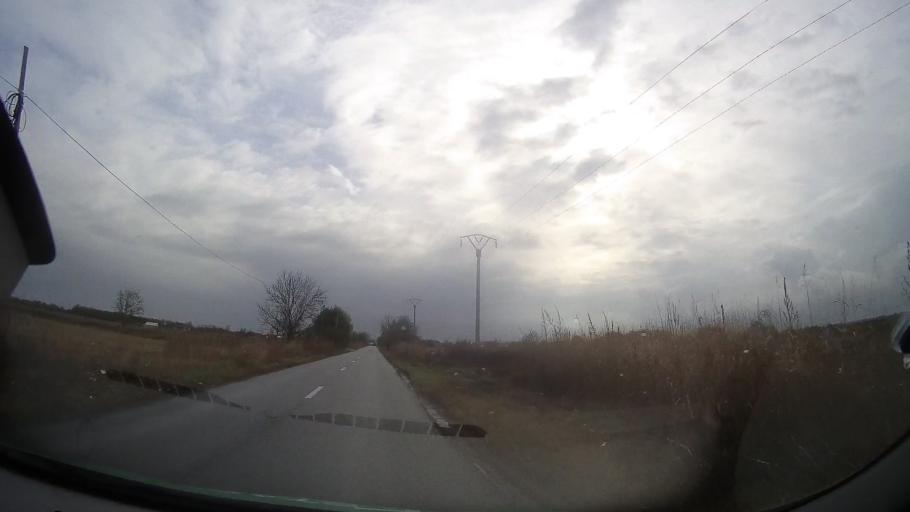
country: RO
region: Ialomita
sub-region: Comuna Fierbinti-Targ
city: Fierbintii de Jos
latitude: 44.7040
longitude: 26.3929
